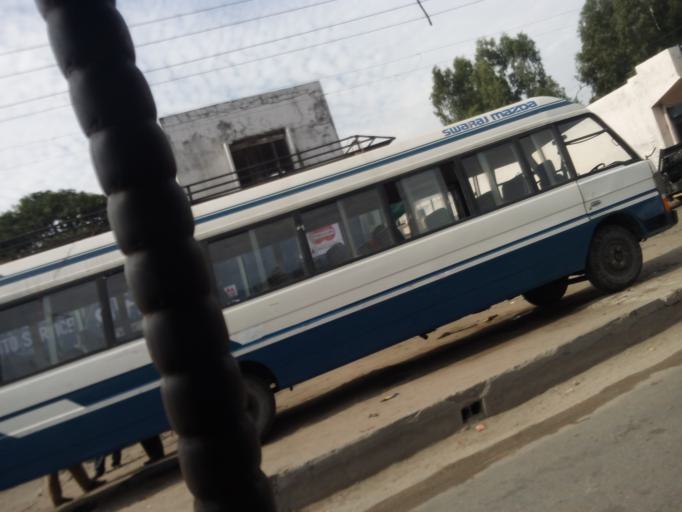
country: IN
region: Punjab
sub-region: Hoshiarpur
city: Hoshiarpur
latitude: 31.5281
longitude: 75.8965
